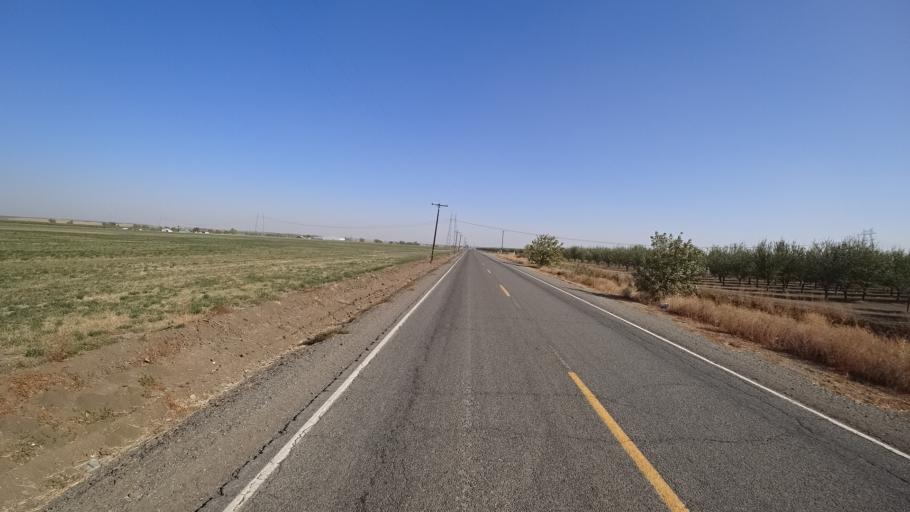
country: US
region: California
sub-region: Yolo County
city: Cottonwood
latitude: 38.7182
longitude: -121.9488
